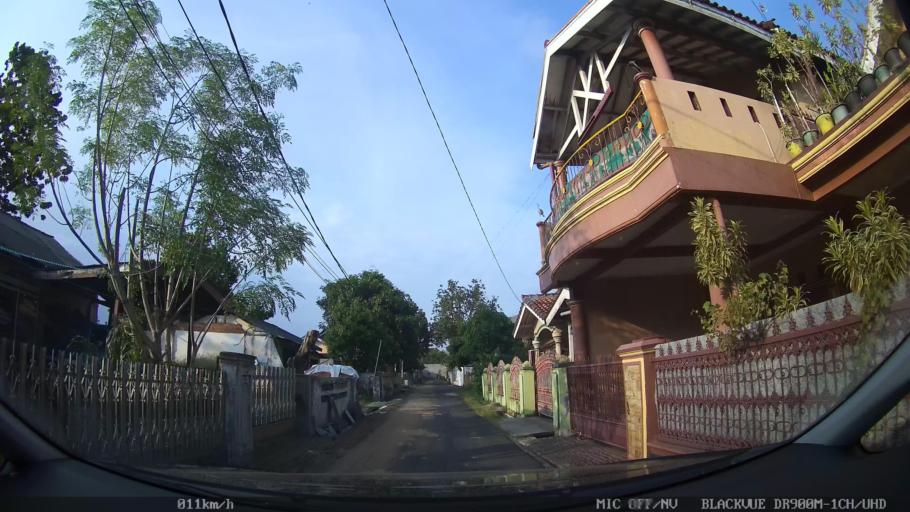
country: ID
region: Lampung
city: Kedaton
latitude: -5.3976
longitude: 105.2989
